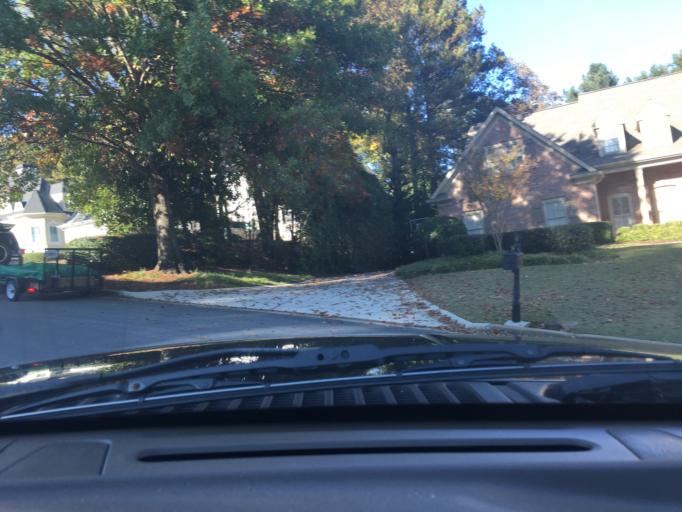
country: US
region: Georgia
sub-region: Fulton County
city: Johns Creek
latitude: 34.0292
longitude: -84.1727
